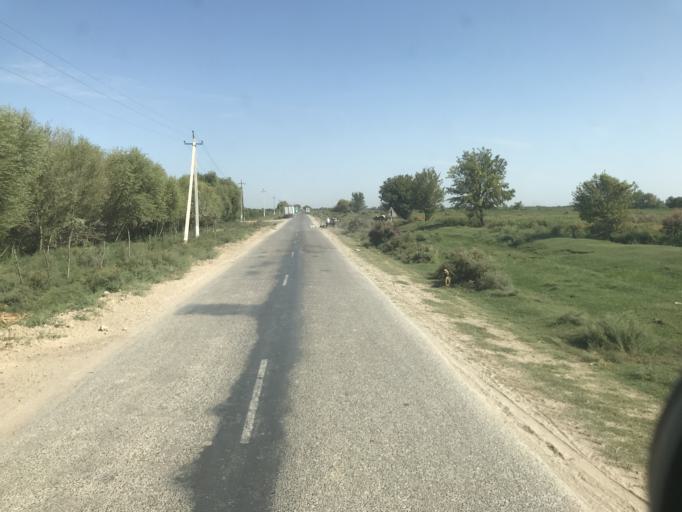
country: KZ
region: Ongtustik Qazaqstan
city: Myrzakent
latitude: 40.6661
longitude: 68.6332
